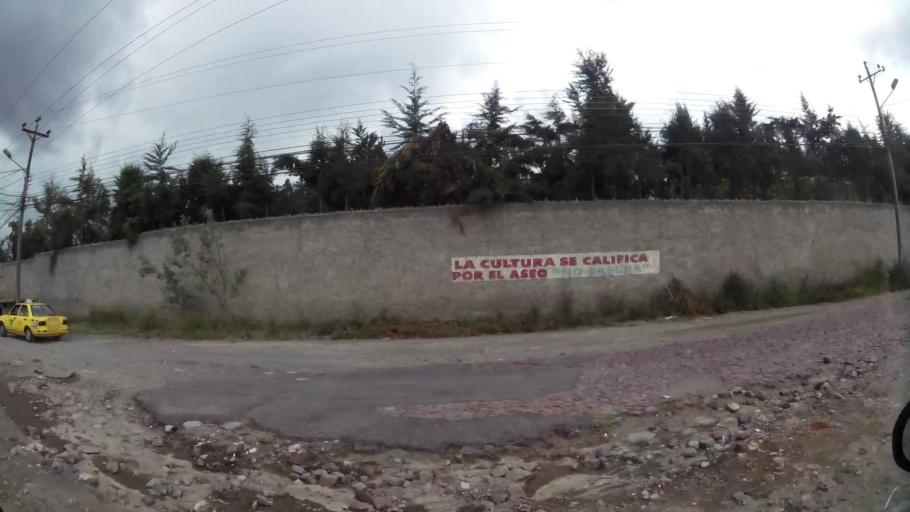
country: EC
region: Pichincha
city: Quito
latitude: -0.0926
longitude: -78.4695
